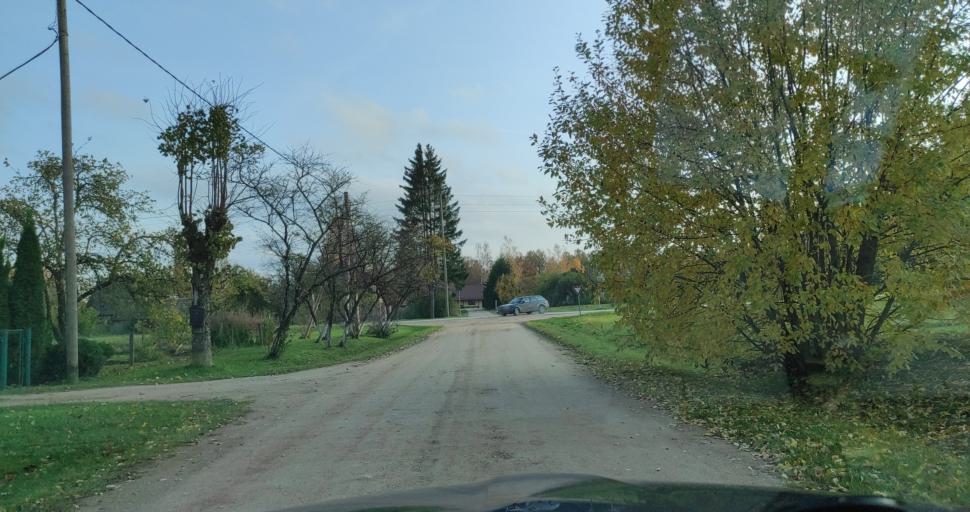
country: LV
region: Vainode
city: Vainode
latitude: 56.4231
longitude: 21.8748
